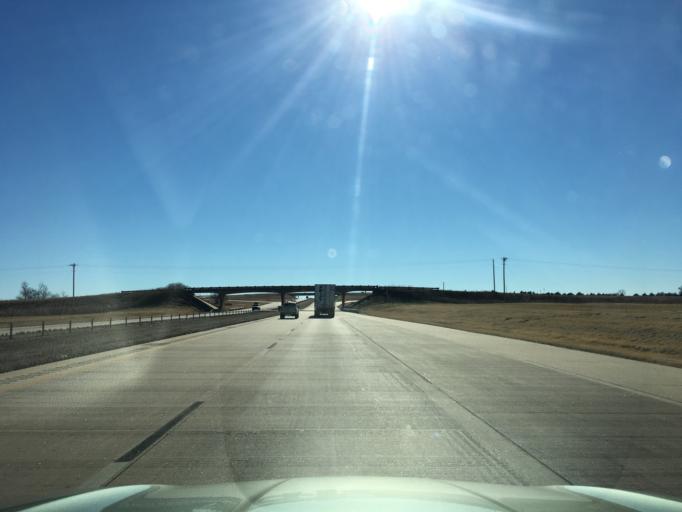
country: US
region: Oklahoma
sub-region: Noble County
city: Perry
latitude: 36.4076
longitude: -97.3272
